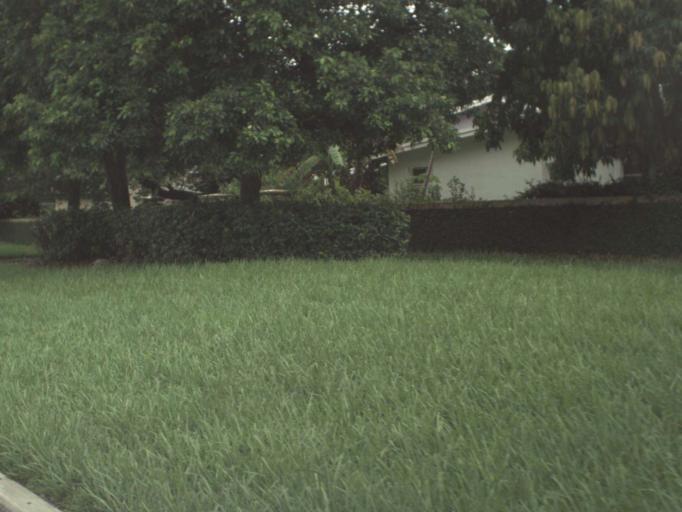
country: US
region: Florida
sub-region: Miami-Dade County
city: Coral Gables
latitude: 25.7303
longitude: -80.2568
